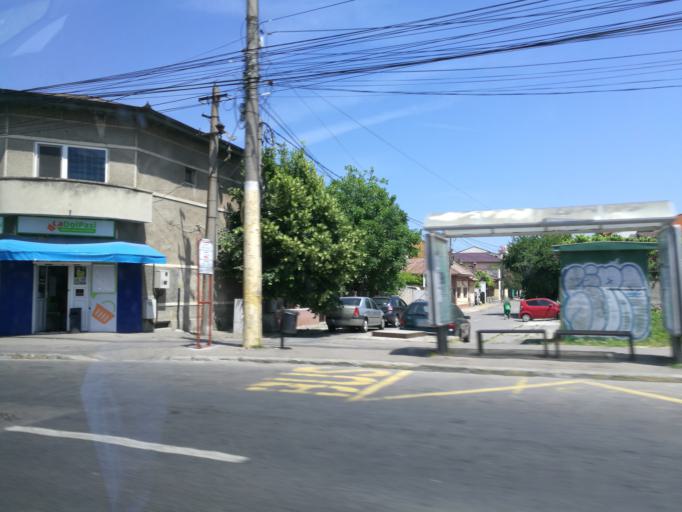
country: RO
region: Constanta
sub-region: Municipiul Constanta
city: Constanta
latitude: 44.1973
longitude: 28.6482
